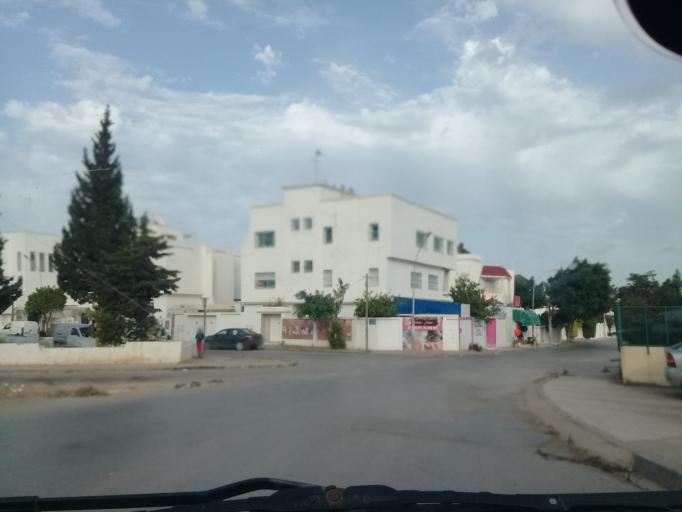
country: TN
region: Ariana
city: Ariana
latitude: 36.8636
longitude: 10.1693
